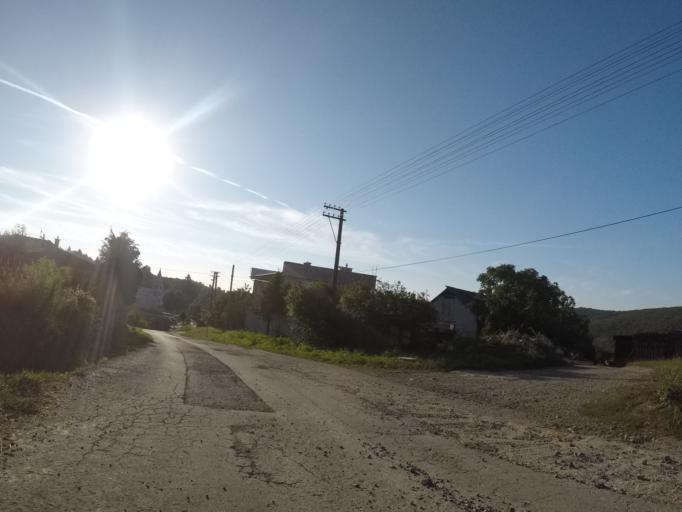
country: SK
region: Kosicky
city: Kosice
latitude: 48.7319
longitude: 21.1399
